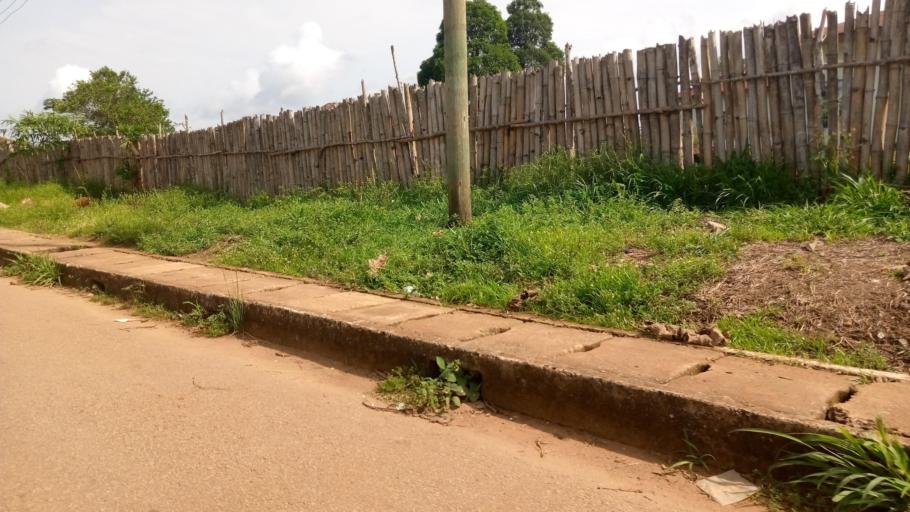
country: SL
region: Southern Province
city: Pujehun
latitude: 7.3580
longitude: -11.7189
